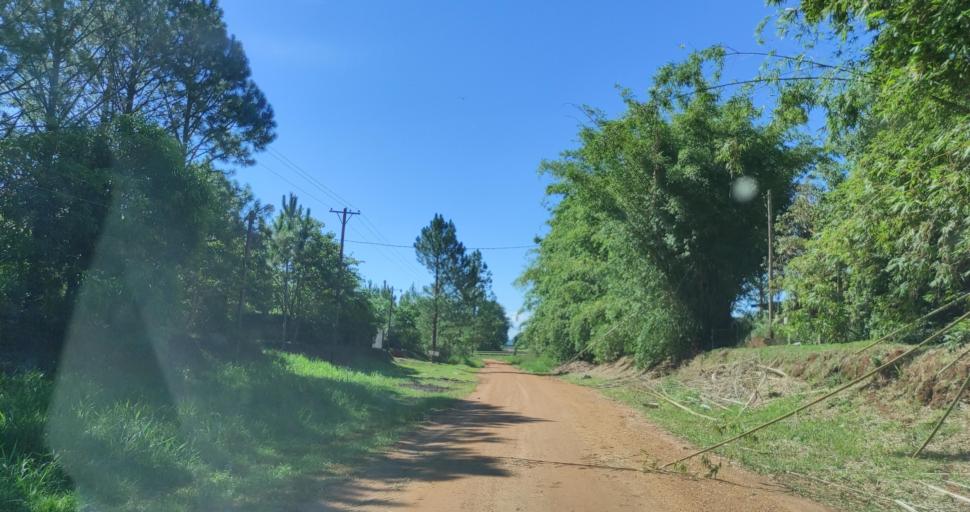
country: AR
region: Misiones
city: Garupa
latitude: -27.4683
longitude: -55.7979
